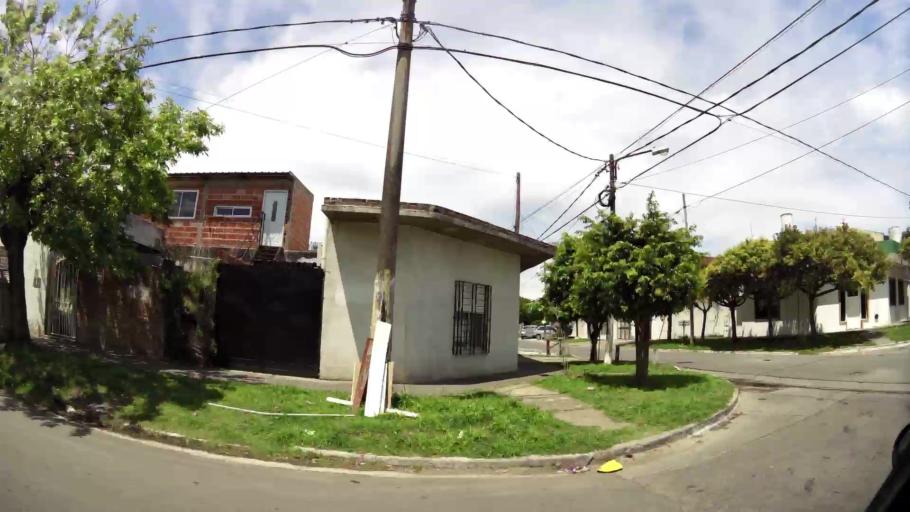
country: AR
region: Buenos Aires
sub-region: Partido de Quilmes
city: Quilmes
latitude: -34.7776
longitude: -58.2592
